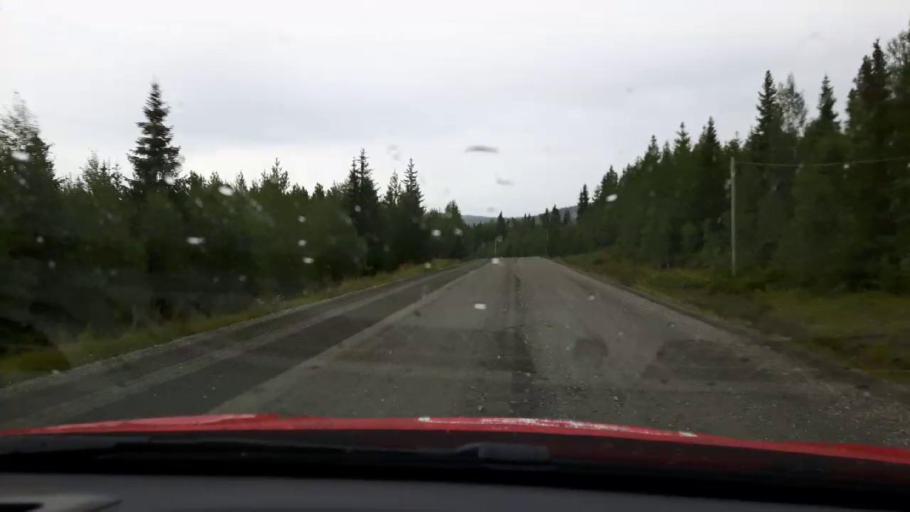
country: SE
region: Jaemtland
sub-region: Are Kommun
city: Are
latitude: 63.4077
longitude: 12.7994
